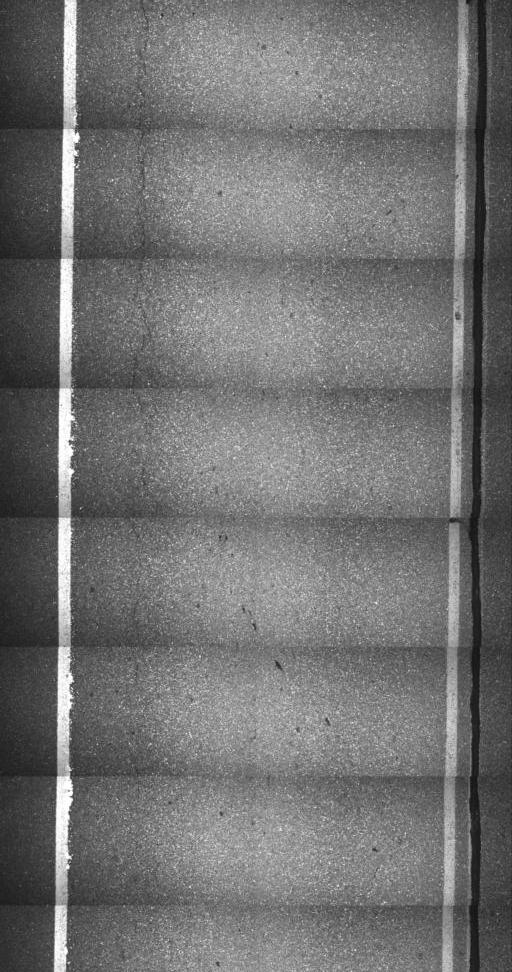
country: CA
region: Quebec
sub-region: Estrie
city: Coaticook
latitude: 45.0054
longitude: -71.7985
